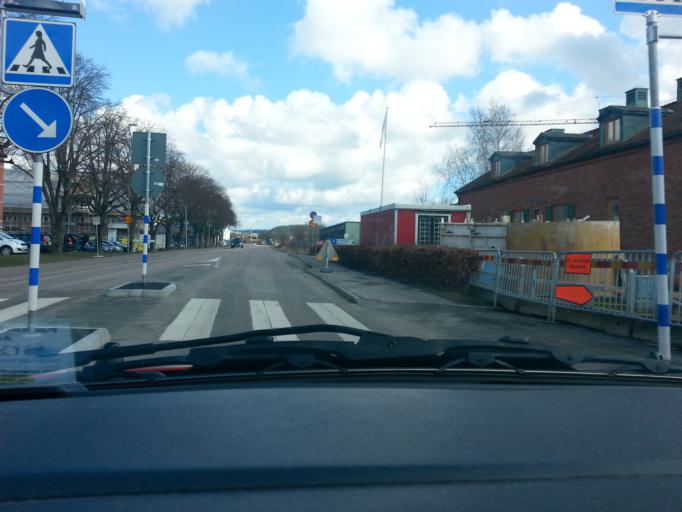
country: SE
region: Vaestra Goetaland
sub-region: Partille Kommun
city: Partille
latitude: 57.7408
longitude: 12.1139
